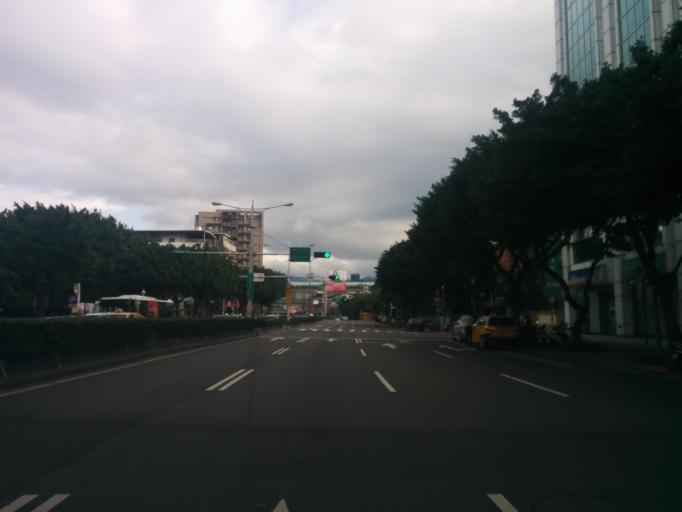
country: TW
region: Taipei
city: Taipei
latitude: 25.0726
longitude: 121.5189
